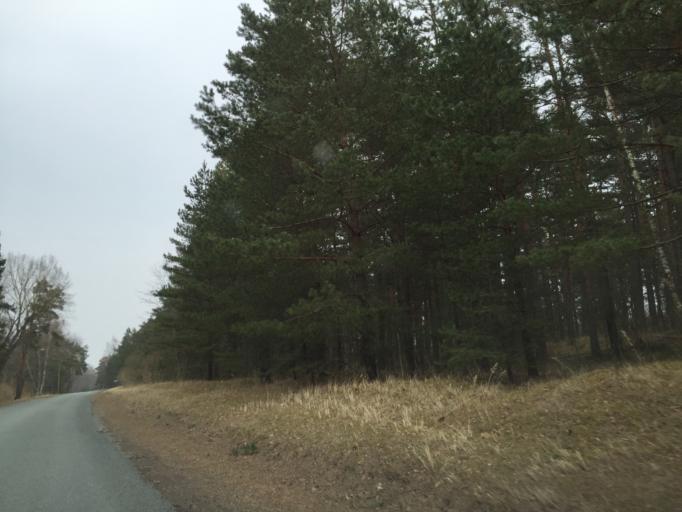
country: LV
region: Salacgrivas
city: Ainazi
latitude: 57.9948
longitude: 24.4296
